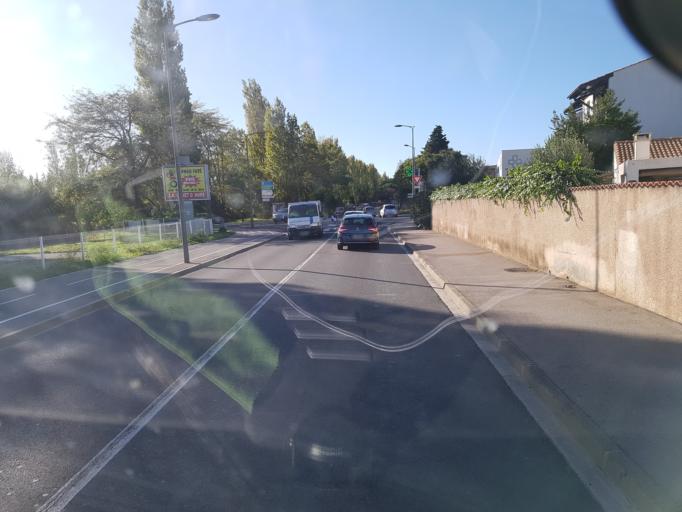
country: FR
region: Languedoc-Roussillon
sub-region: Departement de l'Aude
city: Narbonne
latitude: 43.1750
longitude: 3.0043
